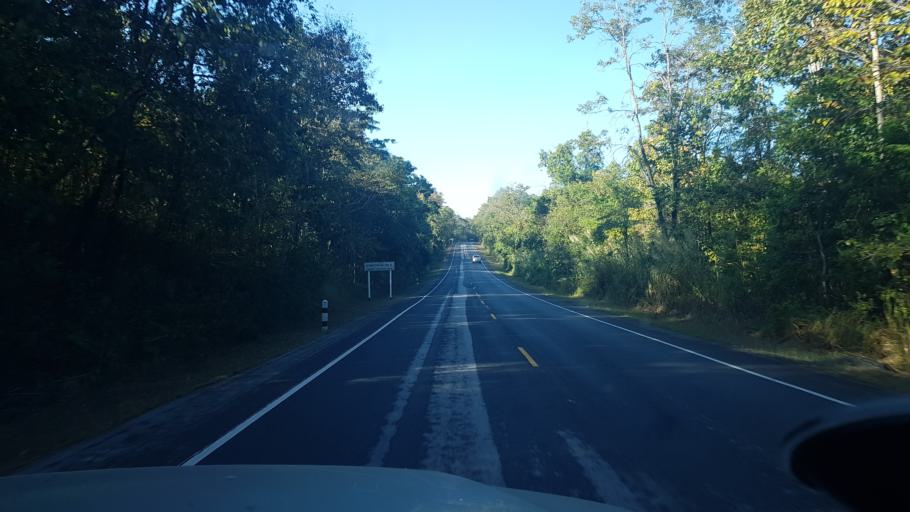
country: TH
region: Phetchabun
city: Lom Sak
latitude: 16.7396
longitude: 101.4440
